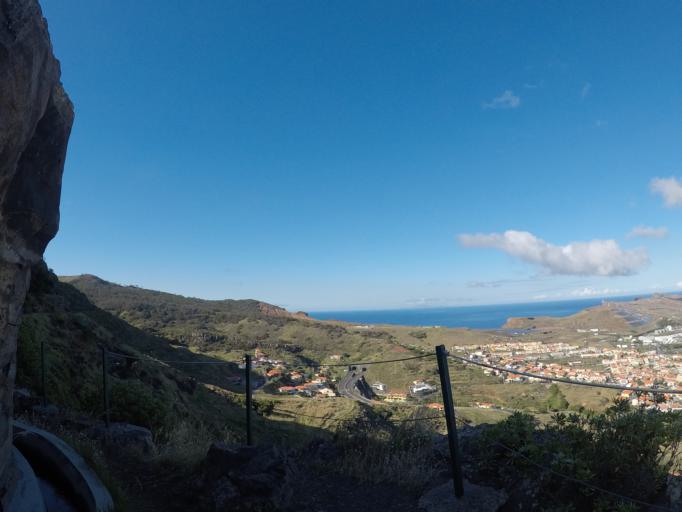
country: PT
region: Madeira
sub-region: Machico
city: Canical
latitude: 32.7399
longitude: -16.7484
